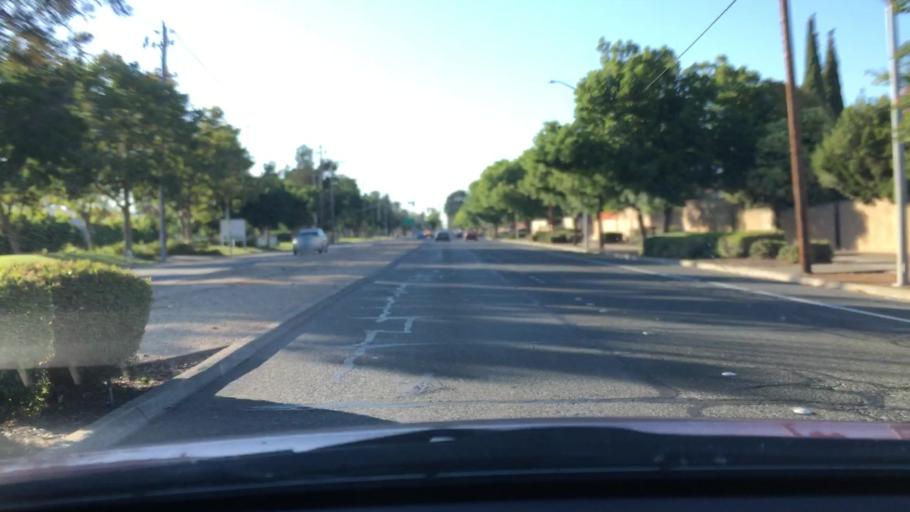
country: US
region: California
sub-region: Santa Clara County
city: Milpitas
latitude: 37.4660
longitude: -121.9157
